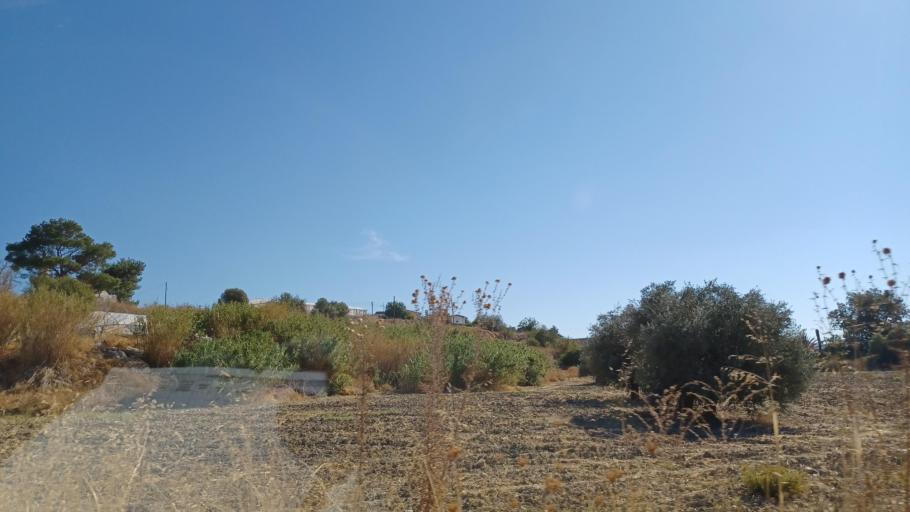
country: CY
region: Pafos
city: Polis
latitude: 35.0050
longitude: 32.4362
